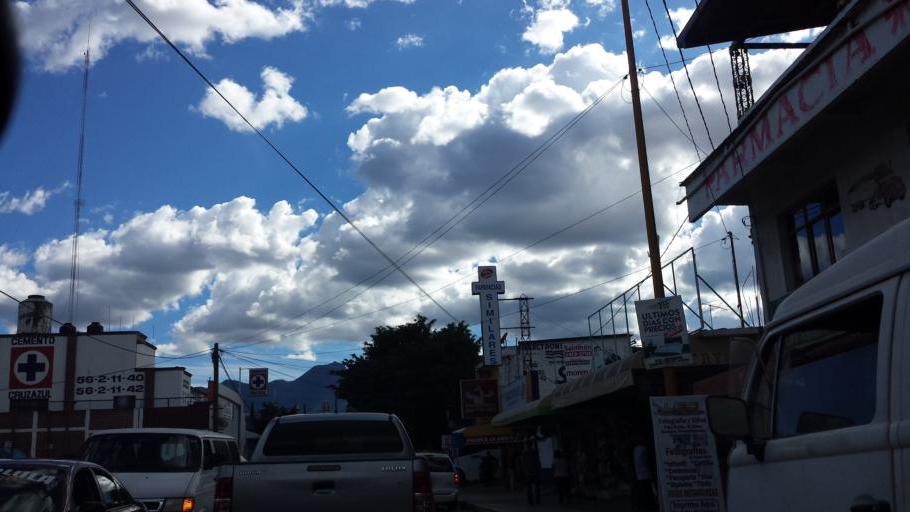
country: MX
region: Oaxaca
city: Tlacolula de Matamoros
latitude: 16.9613
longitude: -96.4772
